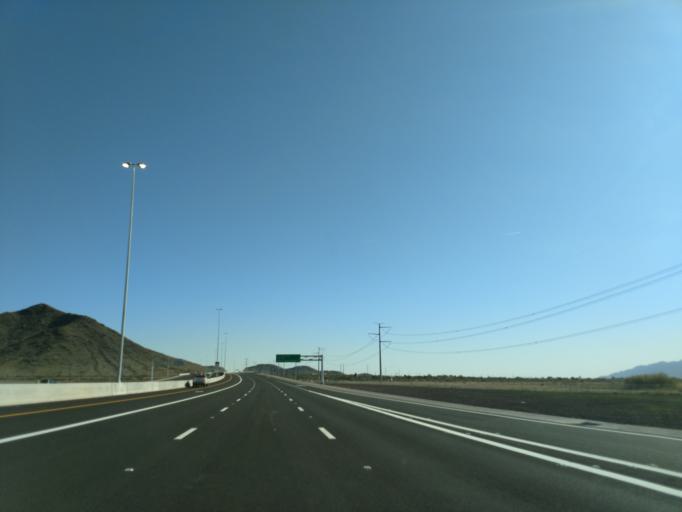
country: US
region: Arizona
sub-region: Maricopa County
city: Laveen
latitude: 33.3306
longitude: -112.1732
